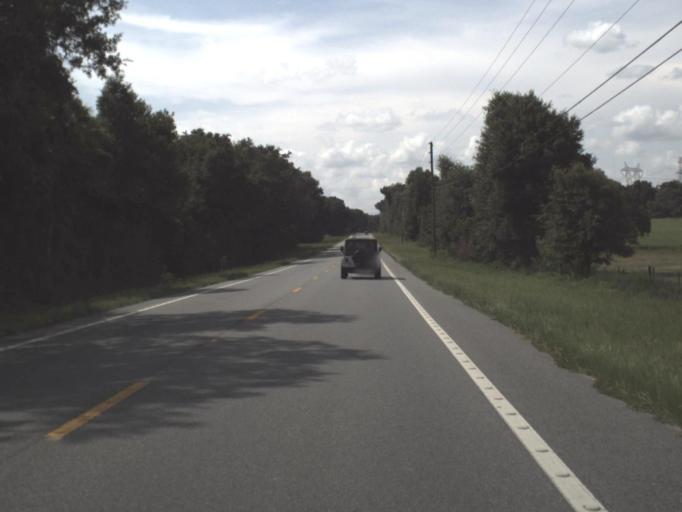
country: US
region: Florida
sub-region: Citrus County
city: Beverly Hills
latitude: 28.9574
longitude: -82.4140
